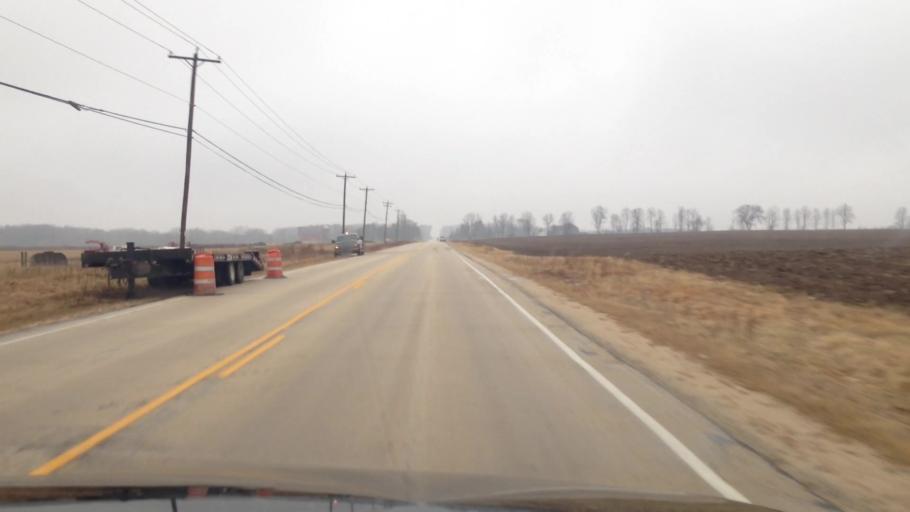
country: US
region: Wisconsin
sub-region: Washington County
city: Richfield
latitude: 43.2525
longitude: -88.1625
